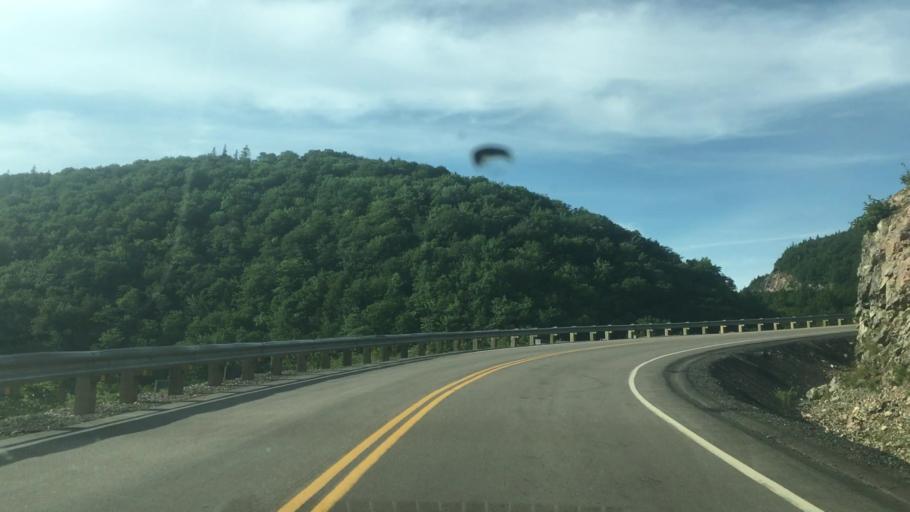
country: CA
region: Nova Scotia
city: Sydney Mines
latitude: 46.8150
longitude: -60.6513
